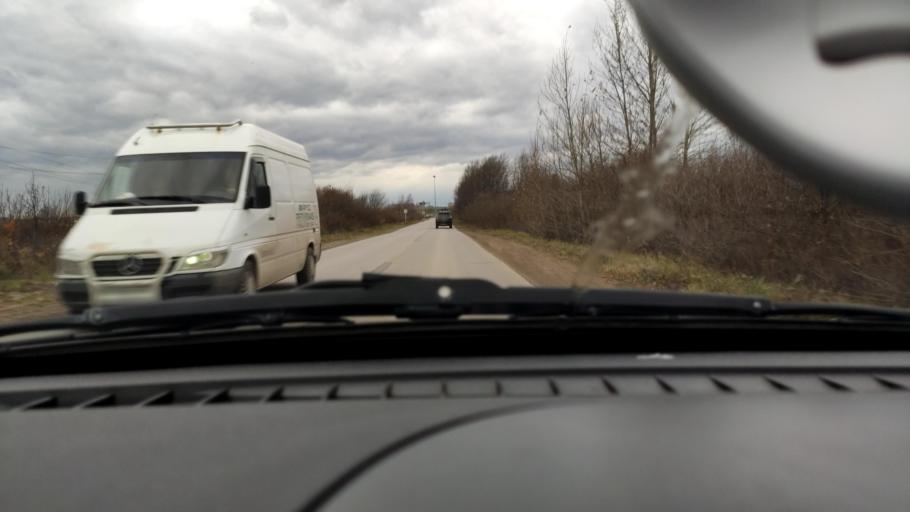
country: RU
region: Perm
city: Kondratovo
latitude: 58.0051
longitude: 56.0579
